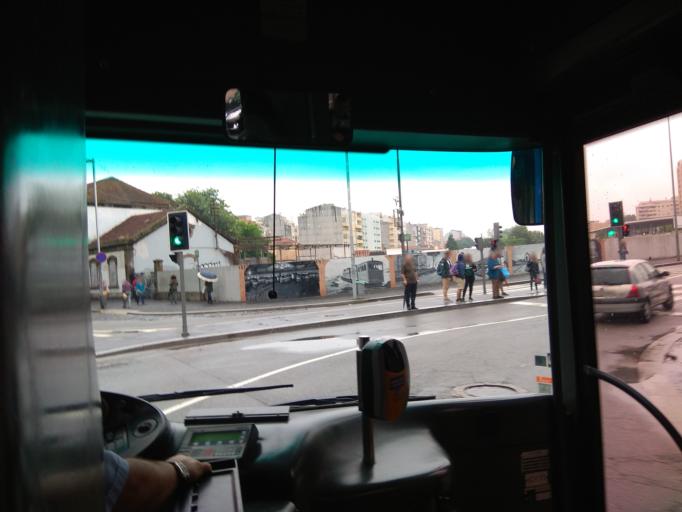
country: PT
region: Porto
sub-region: Porto
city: Porto
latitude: 41.1588
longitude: -8.6287
